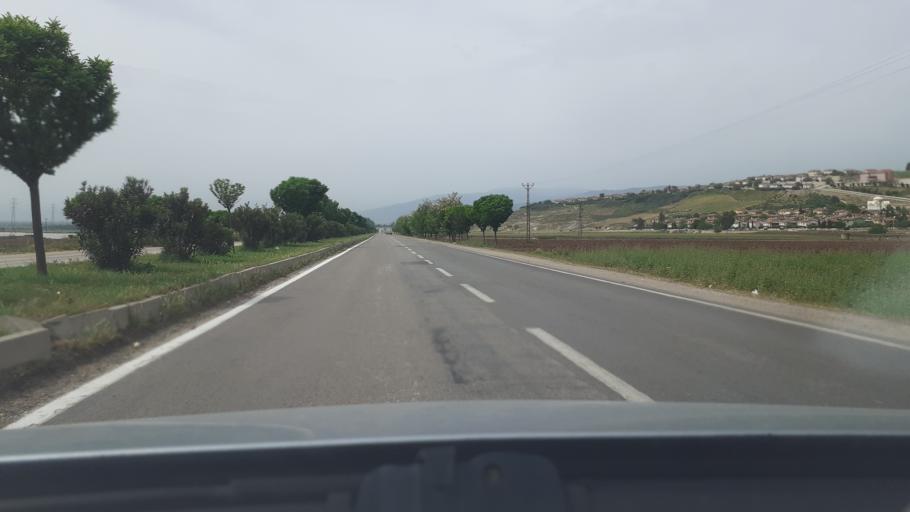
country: TR
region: Hatay
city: Kirikhan
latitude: 36.4772
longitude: 36.3527
